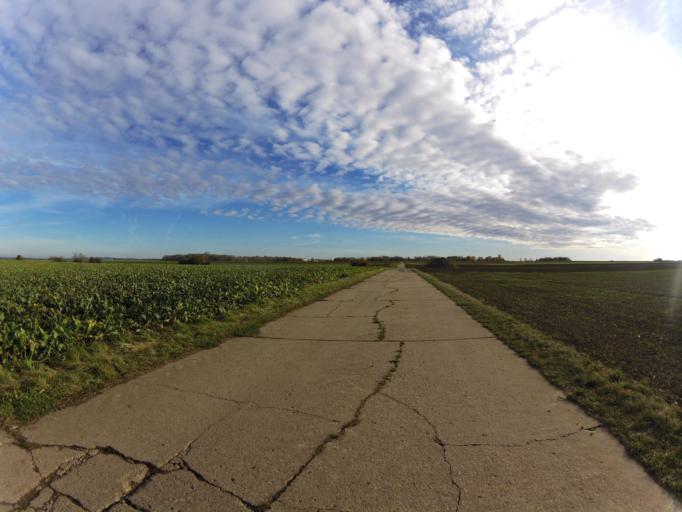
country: DE
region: Bavaria
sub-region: Regierungsbezirk Unterfranken
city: Giebelstadt
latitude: 49.6660
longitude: 9.9653
